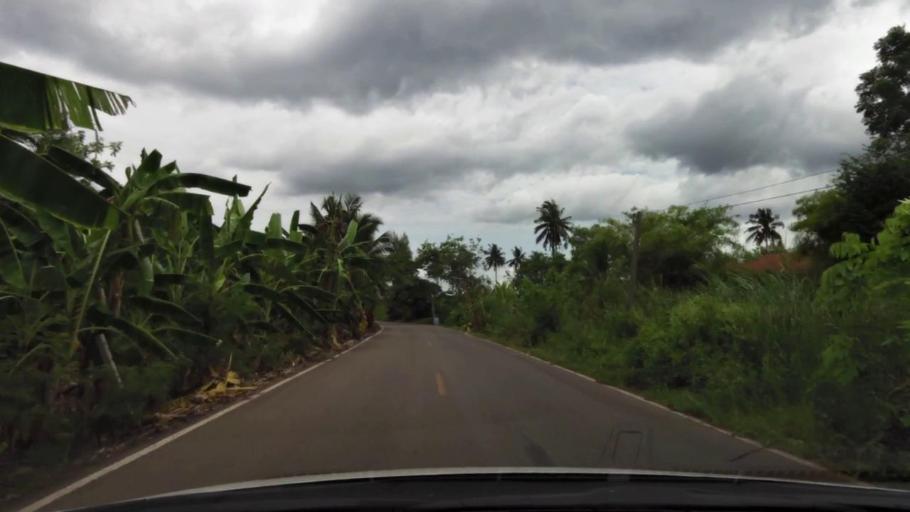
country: TH
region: Samut Sakhon
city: Ban Phaeo
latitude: 13.5634
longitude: 100.0338
